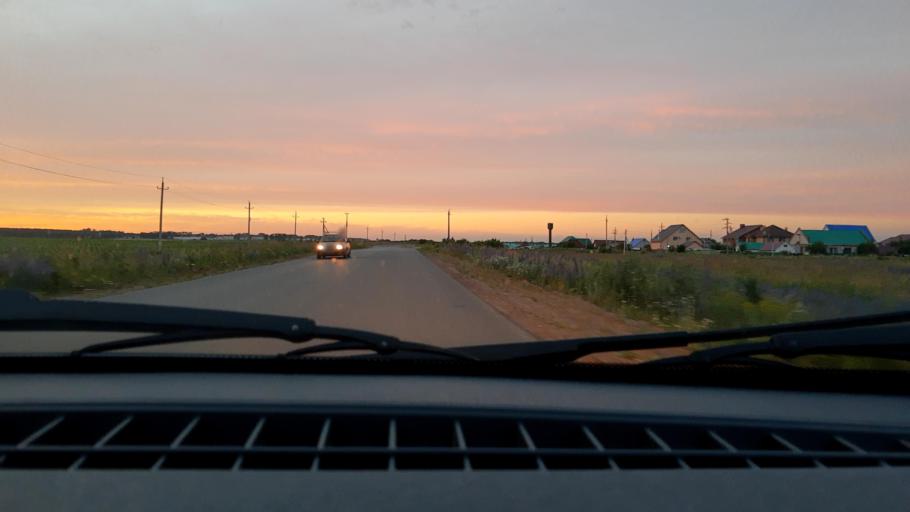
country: RU
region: Bashkortostan
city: Mikhaylovka
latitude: 54.8090
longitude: 55.7836
